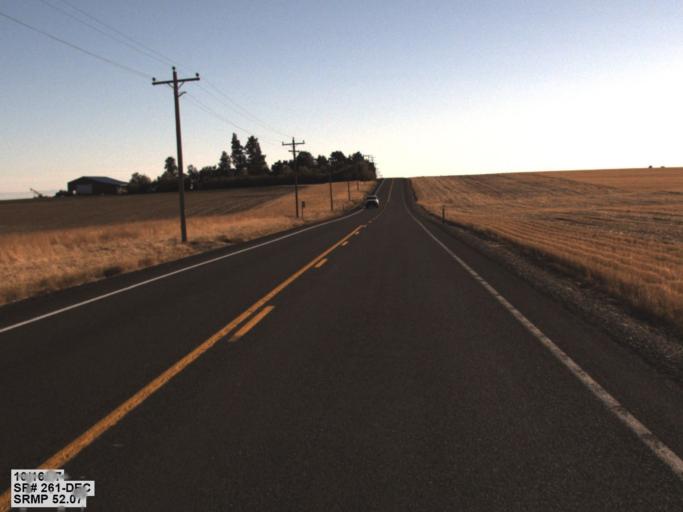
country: US
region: Washington
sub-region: Adams County
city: Ritzville
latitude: 46.9672
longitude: -118.3434
